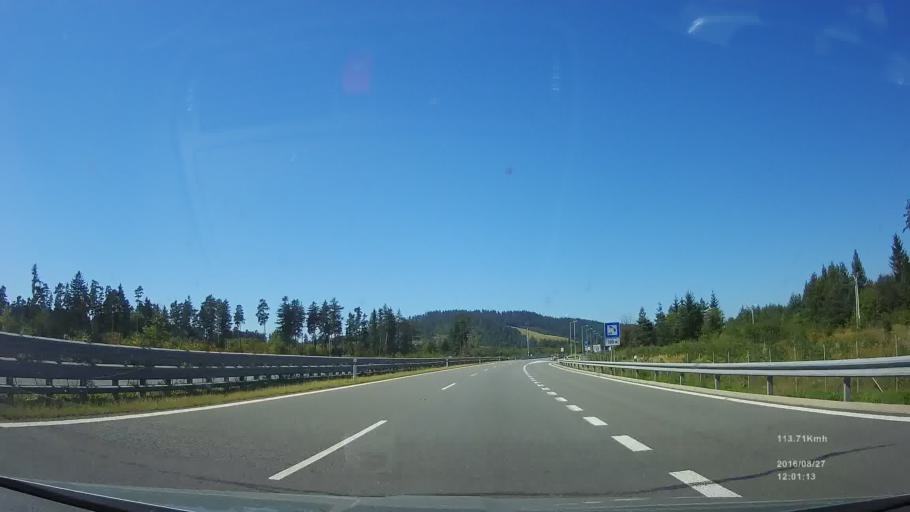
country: SK
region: Presovsky
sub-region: Okres Poprad
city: Svit
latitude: 49.0644
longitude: 20.1864
